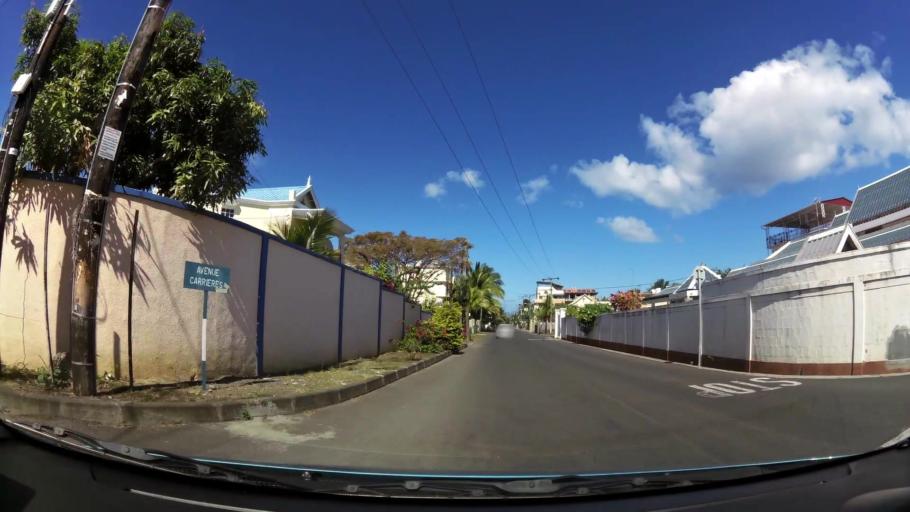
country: MU
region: Black River
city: Flic en Flac
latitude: -20.2854
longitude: 57.3676
